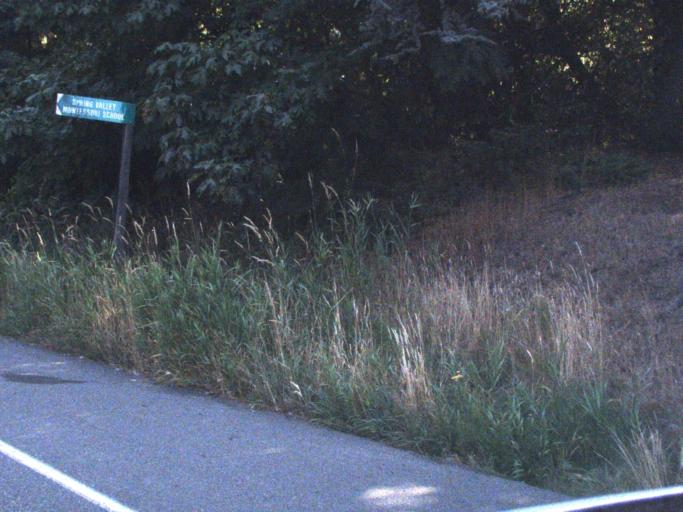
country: US
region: Washington
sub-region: Pierce County
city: Fife Heights
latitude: 47.2737
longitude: -122.3283
